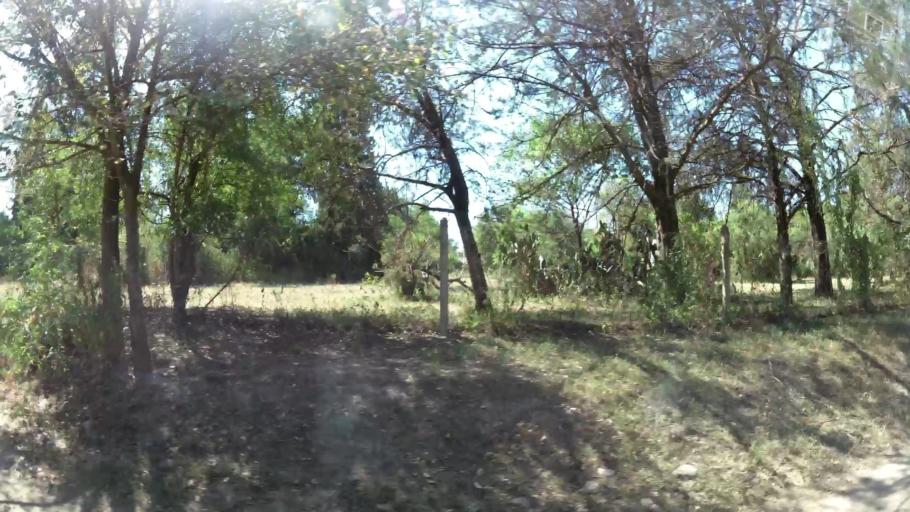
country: AR
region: Cordoba
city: Mendiolaza
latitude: -31.2687
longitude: -64.3004
